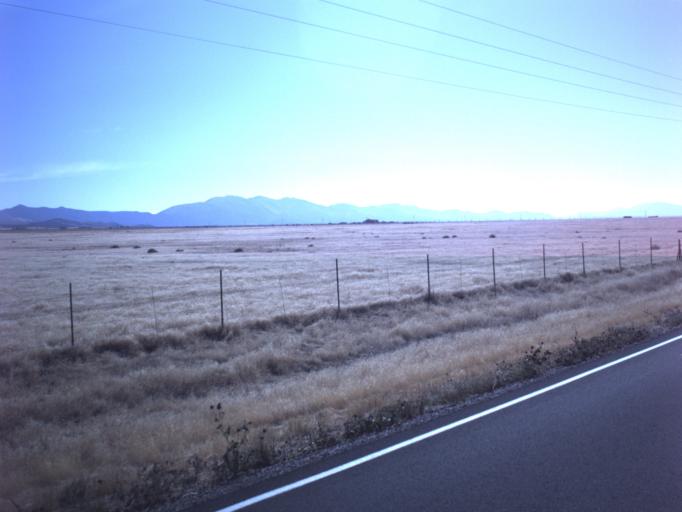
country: US
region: Utah
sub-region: Tooele County
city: Grantsville
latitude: 40.4091
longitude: -112.7484
